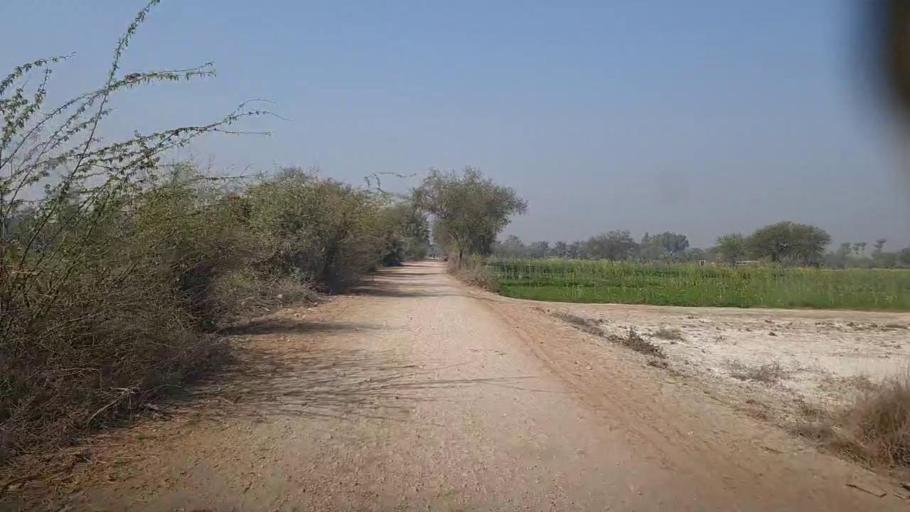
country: PK
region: Sindh
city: Karaundi
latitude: 26.8459
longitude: 68.3858
